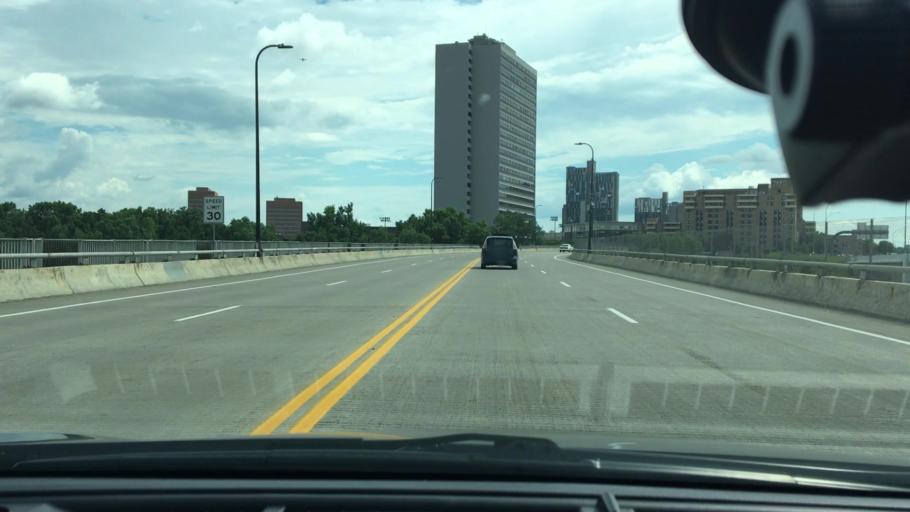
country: US
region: Minnesota
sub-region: Hennepin County
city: Minneapolis
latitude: 44.9786
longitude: -93.2441
